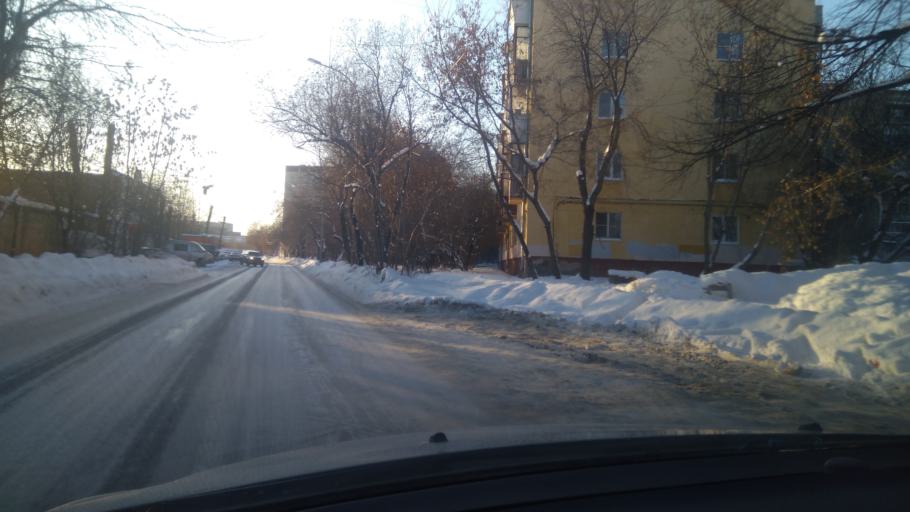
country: RU
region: Sverdlovsk
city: Yekaterinburg
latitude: 56.8827
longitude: 60.5701
